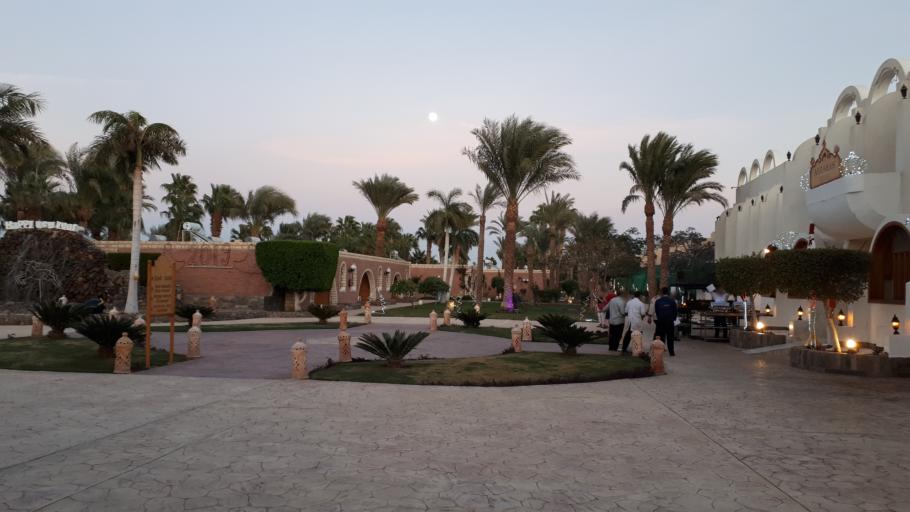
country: EG
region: Red Sea
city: Makadi Bay
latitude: 27.1060
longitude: 33.8295
